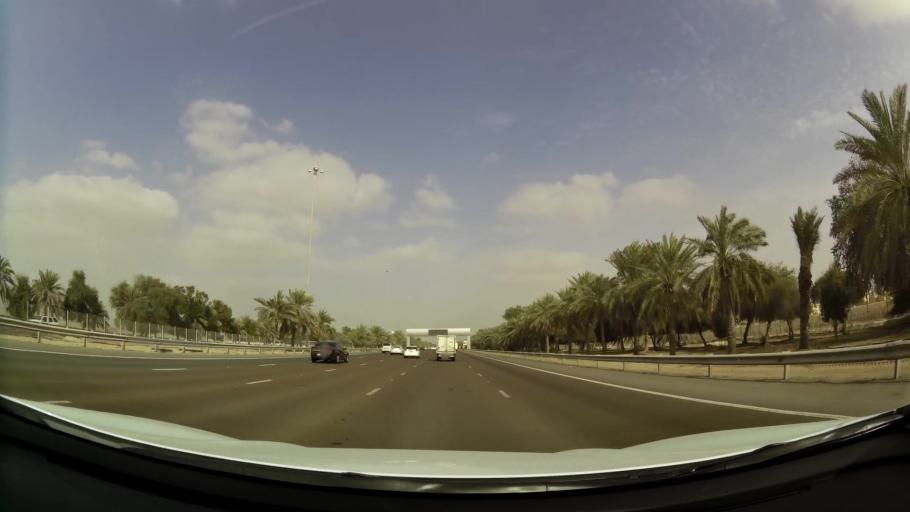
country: AE
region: Abu Dhabi
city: Abu Dhabi
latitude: 24.4302
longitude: 54.5486
